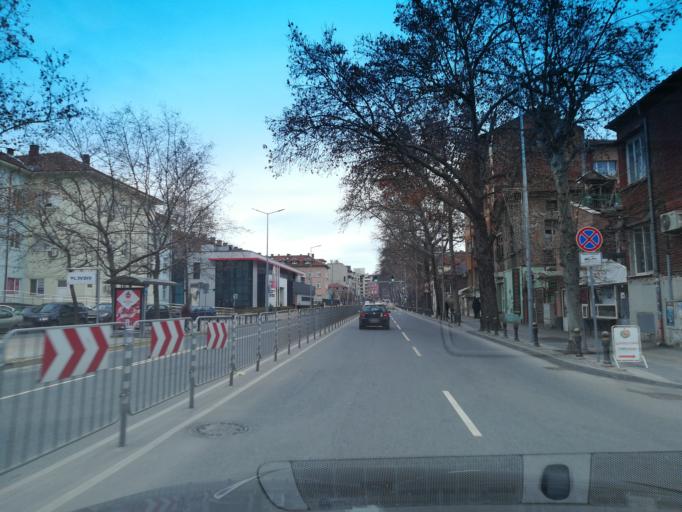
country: BG
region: Plovdiv
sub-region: Obshtina Plovdiv
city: Plovdiv
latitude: 42.1395
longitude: 24.7374
